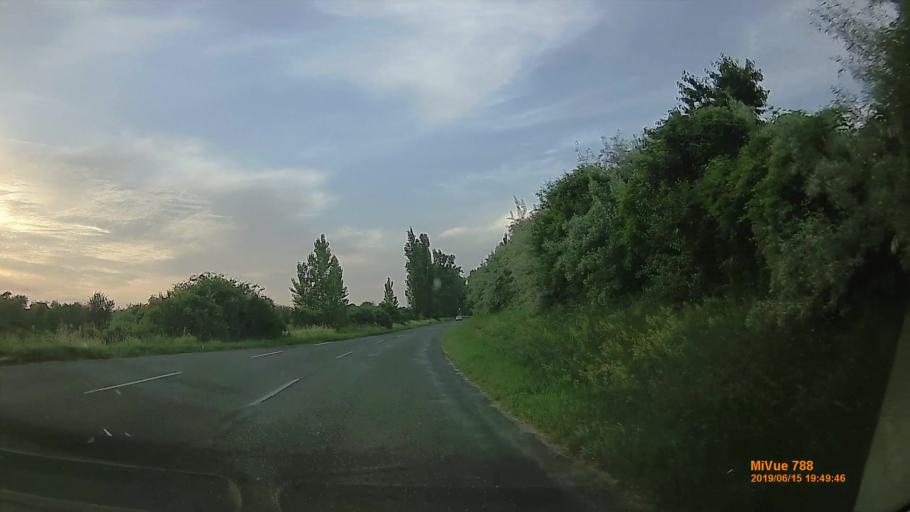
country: HU
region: Veszprem
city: Szentkiralyszabadja
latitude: 47.0387
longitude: 17.9309
